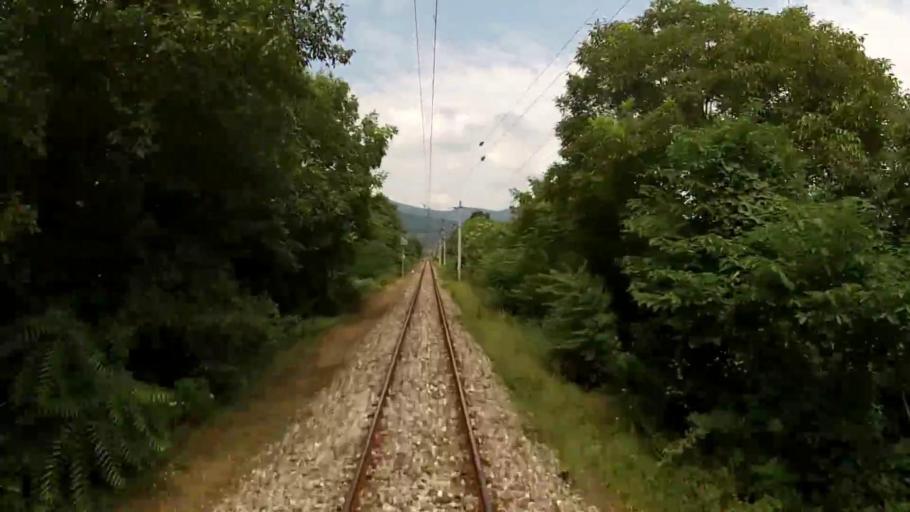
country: BG
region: Blagoevgrad
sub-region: Obshtina Simitli
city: Simitli
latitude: 41.8669
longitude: 23.1229
